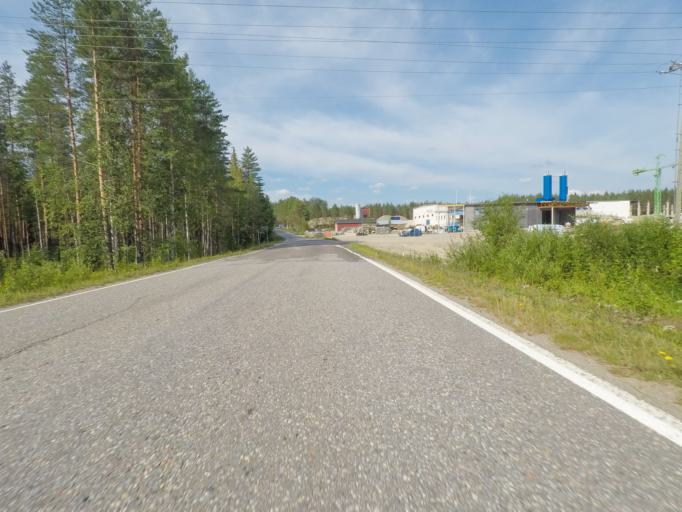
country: FI
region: Southern Savonia
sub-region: Savonlinna
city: Sulkava
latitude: 61.7857
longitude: 28.2425
